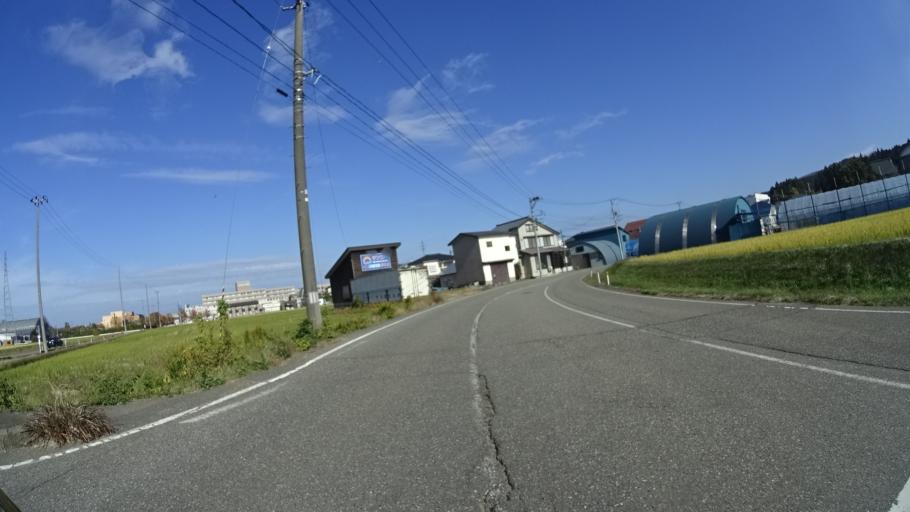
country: JP
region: Niigata
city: Itoigawa
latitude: 37.0447
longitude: 137.8886
